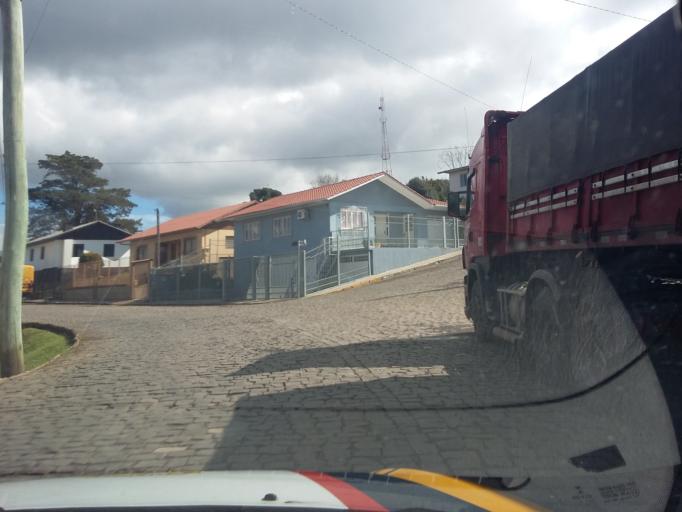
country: BR
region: Rio Grande do Sul
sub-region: Sao Marcos
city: Sao Marcos
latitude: -28.7982
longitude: -51.0923
